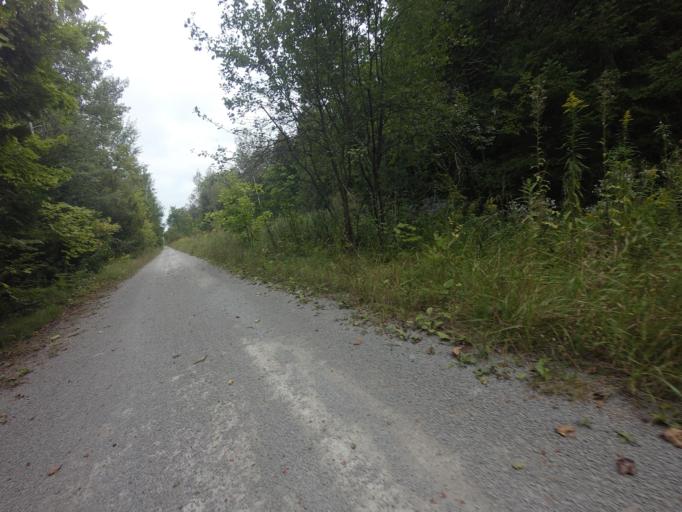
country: CA
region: Ontario
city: Uxbridge
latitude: 44.2662
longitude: -79.0225
